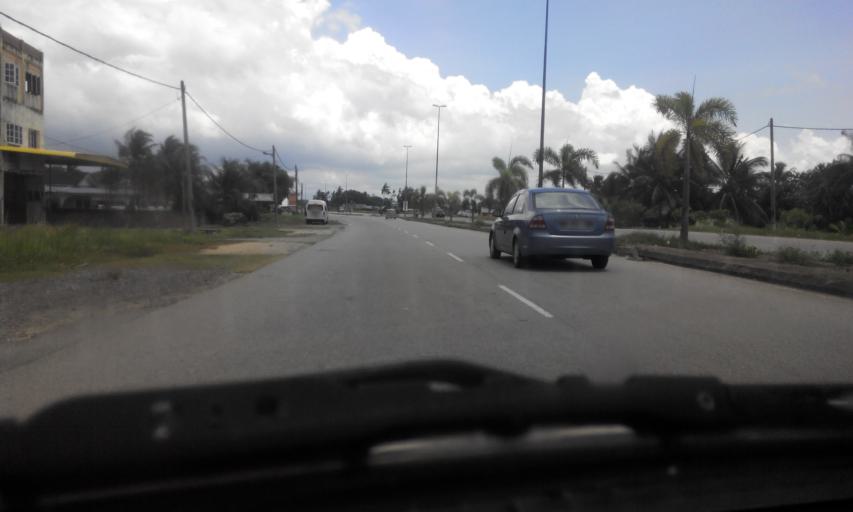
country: MY
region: Perak
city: Parit Buntar
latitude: 5.1291
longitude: 100.5017
